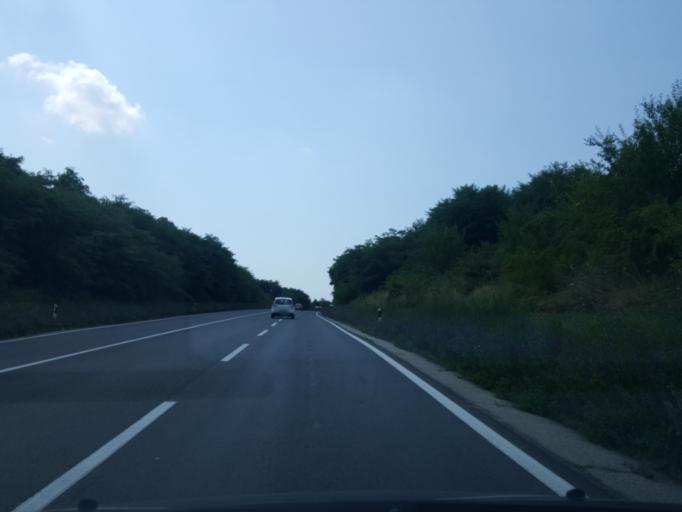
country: RS
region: Central Serbia
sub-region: Belgrade
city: Sopot
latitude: 44.5437
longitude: 20.6584
